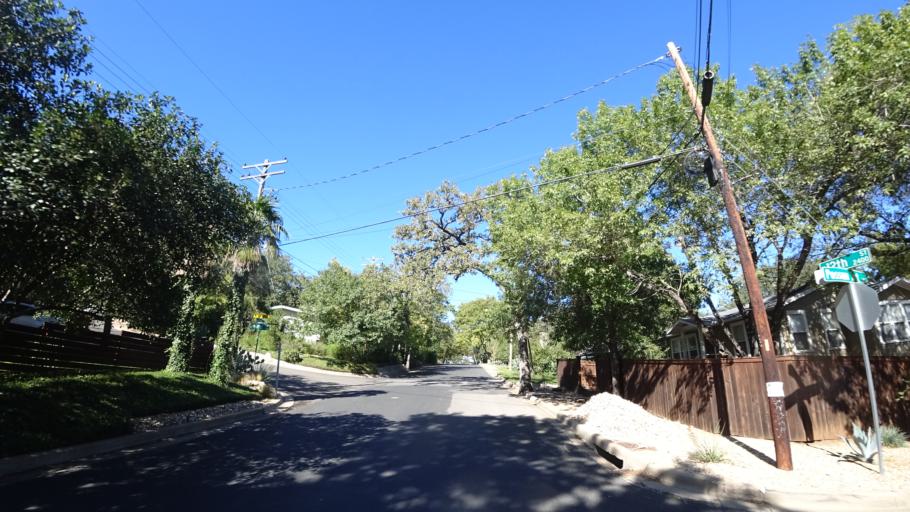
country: US
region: Texas
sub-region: Travis County
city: Rollingwood
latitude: 30.2860
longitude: -97.7707
